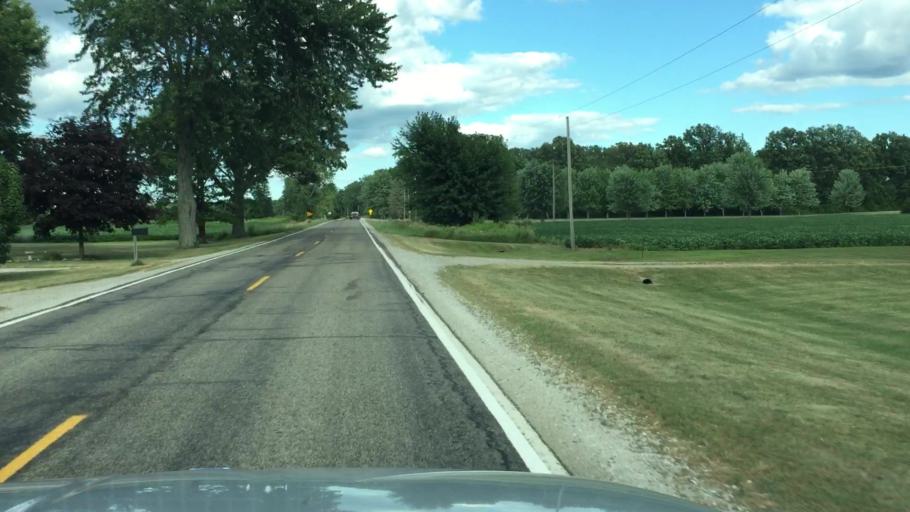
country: US
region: Michigan
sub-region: Saint Clair County
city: Yale
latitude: 43.1281
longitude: -82.8776
